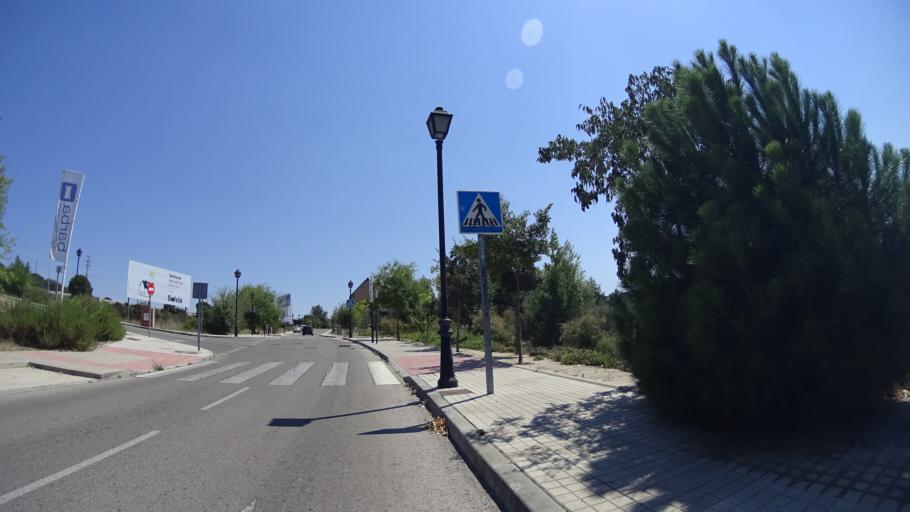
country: ES
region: Madrid
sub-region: Provincia de Madrid
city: Torrelodones
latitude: 40.5780
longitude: -3.9462
